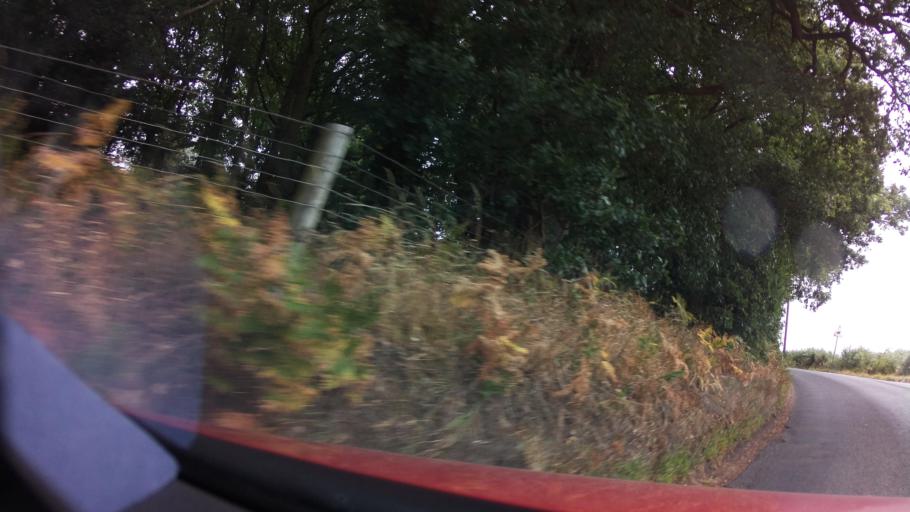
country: GB
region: England
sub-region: Derbyshire
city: Swadlincote
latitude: 52.7957
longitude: -1.5390
